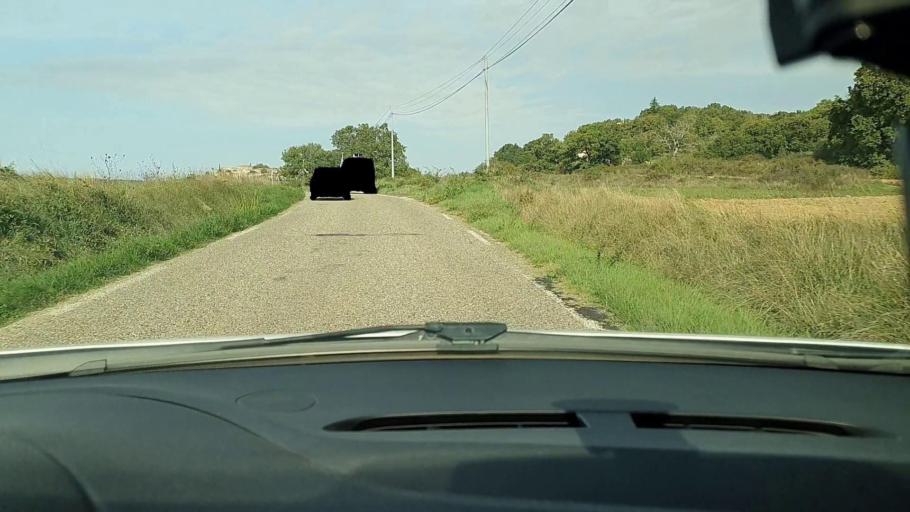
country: FR
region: Languedoc-Roussillon
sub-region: Departement du Gard
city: Goudargues
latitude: 44.1464
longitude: 4.3802
